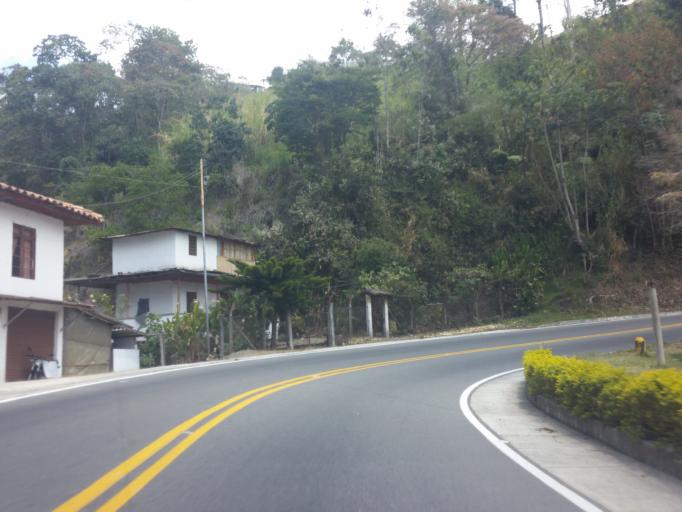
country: CO
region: Caldas
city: Villamaria
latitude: 5.0119
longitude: -75.5487
